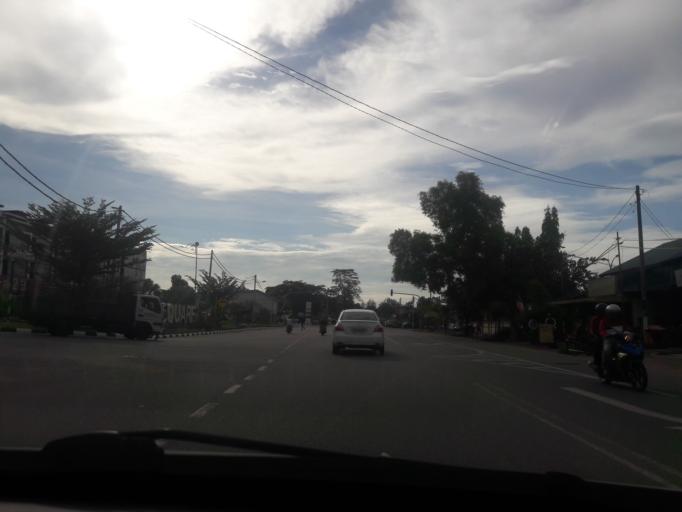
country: MY
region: Kedah
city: Sungai Petani
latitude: 5.6348
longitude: 100.5150
